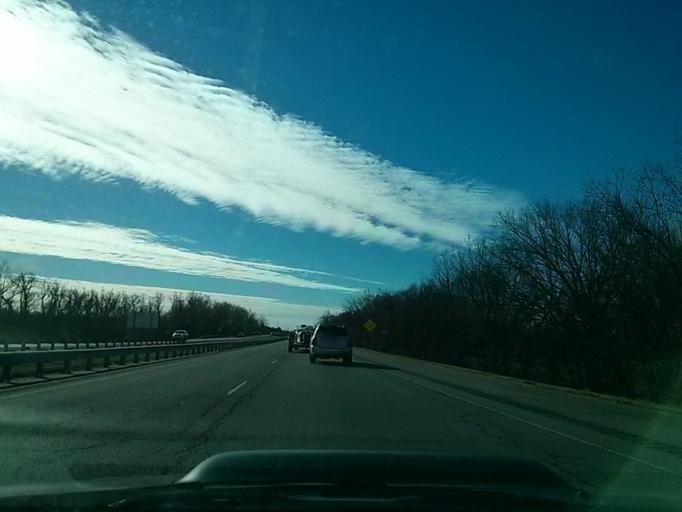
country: US
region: Oklahoma
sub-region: Tulsa County
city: Jenks
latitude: 36.0196
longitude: -96.0119
